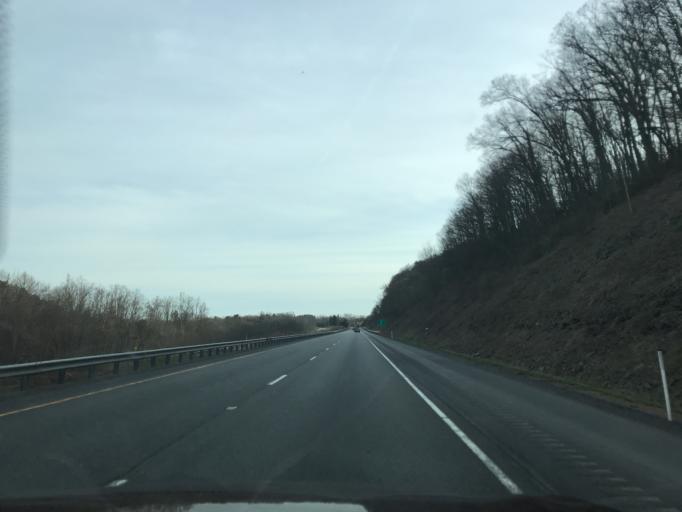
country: US
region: Pennsylvania
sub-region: Lycoming County
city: Muncy
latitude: 41.1556
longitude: -76.7990
